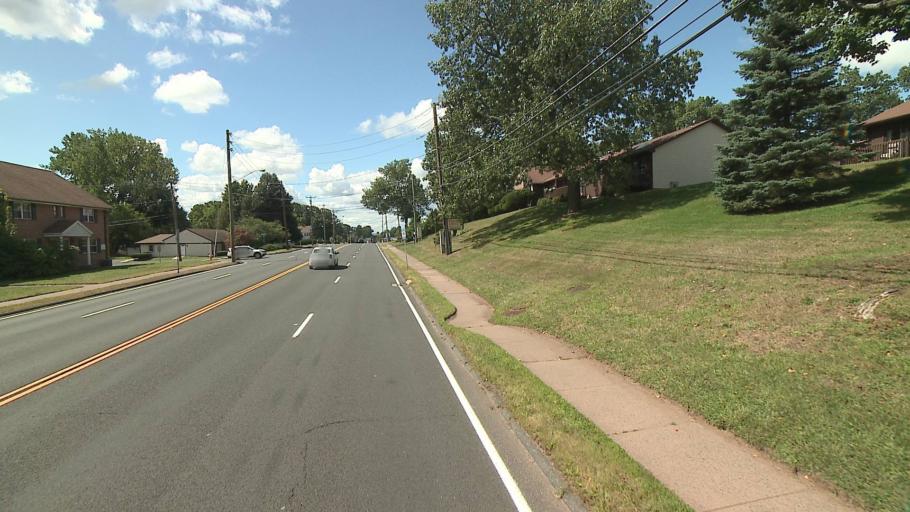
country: US
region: Connecticut
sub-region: Hartford County
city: Manchester
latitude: 41.7856
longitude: -72.4924
